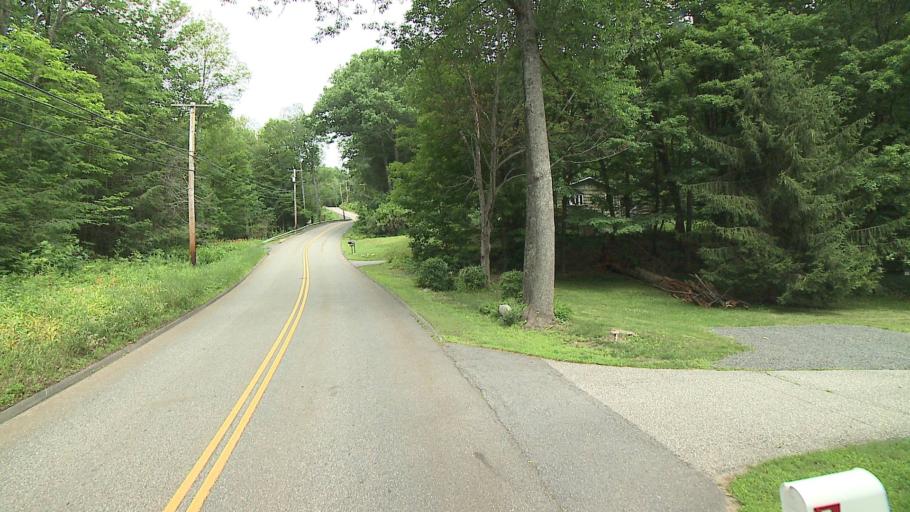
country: US
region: Connecticut
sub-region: Litchfield County
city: Winchester Center
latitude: 41.8690
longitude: -73.0861
